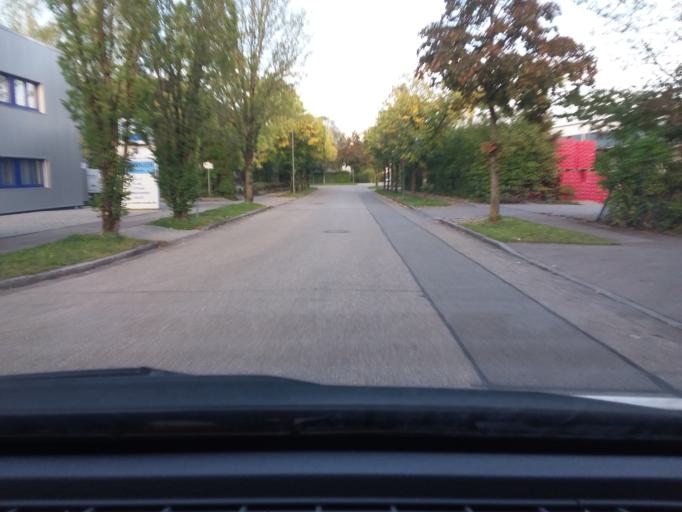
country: DE
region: Bavaria
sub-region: Upper Bavaria
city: Oberschleissheim
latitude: 48.2517
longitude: 11.6056
